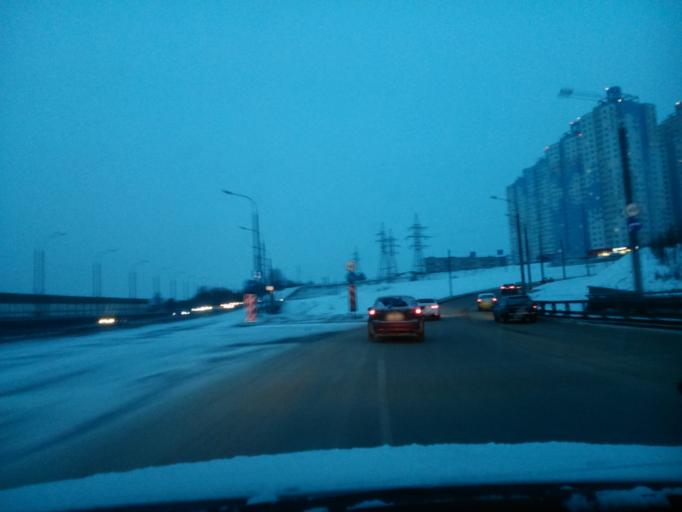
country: RU
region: Perm
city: Perm
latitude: 58.0035
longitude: 56.3167
